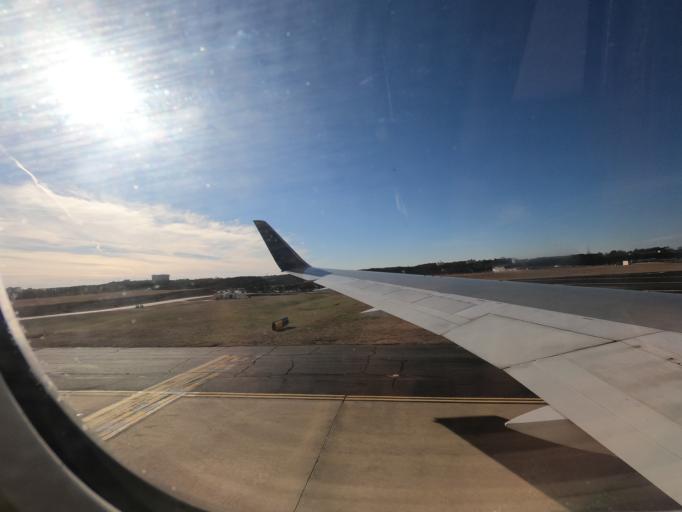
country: US
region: Georgia
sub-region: Fulton County
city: College Park
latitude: 33.6342
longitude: -84.4478
